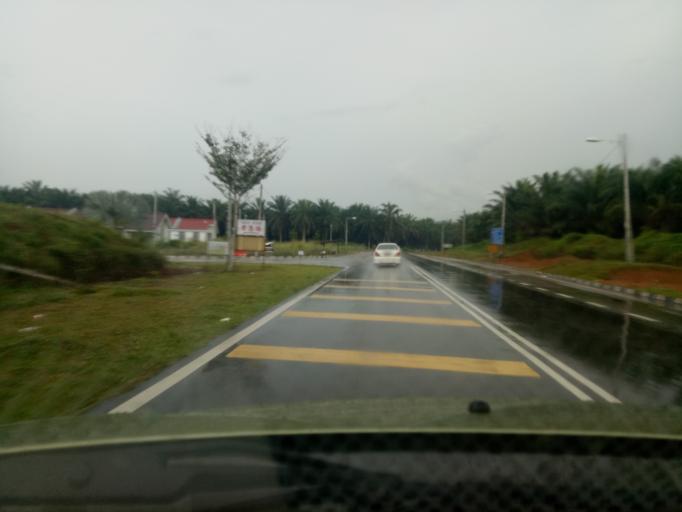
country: MY
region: Penang
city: Tasek Glugor
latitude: 5.5083
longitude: 100.5768
